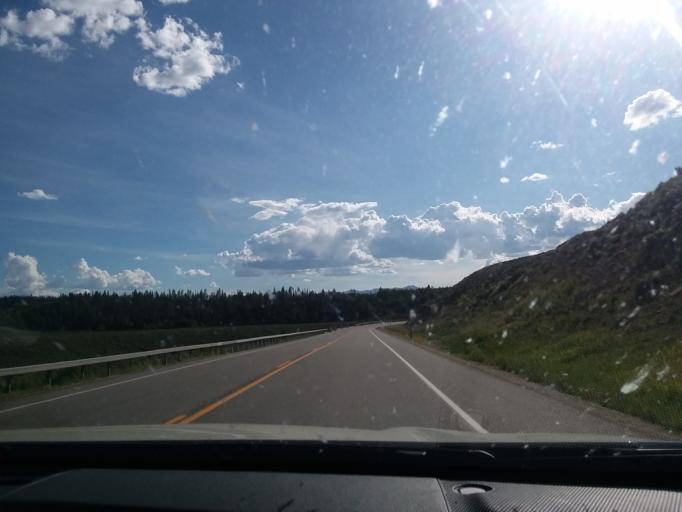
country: US
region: Wyoming
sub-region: Sublette County
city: Pinedale
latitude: 43.1492
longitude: -110.2631
